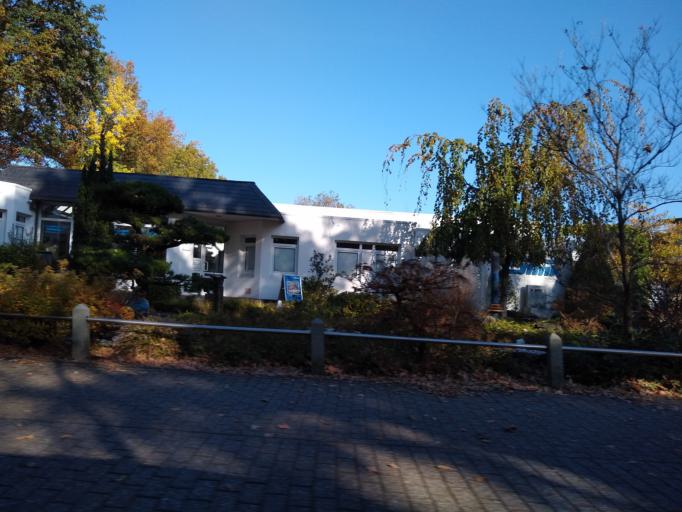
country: DE
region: Lower Saxony
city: Oldenburg
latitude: 53.1850
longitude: 8.2201
